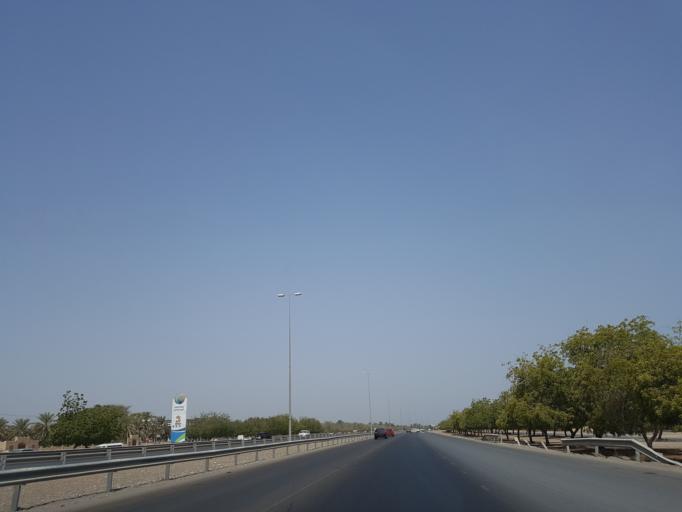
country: OM
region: Al Batinah
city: Saham
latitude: 24.0854
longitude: 56.9341
